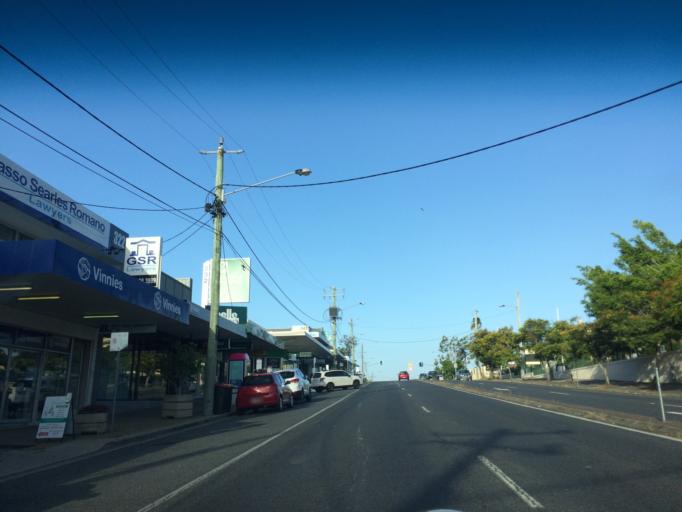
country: AU
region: Queensland
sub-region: Brisbane
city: Camp Hill
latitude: -27.4944
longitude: 153.0595
